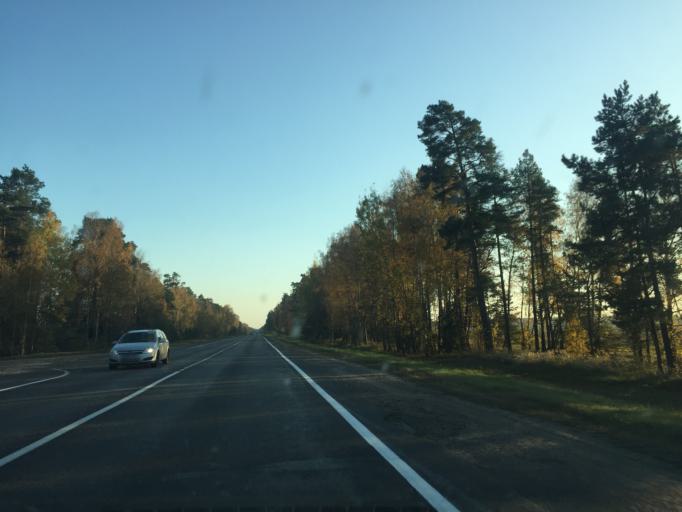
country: BY
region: Mogilev
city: Poselok Voskhod
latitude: 53.7282
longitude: 30.3669
